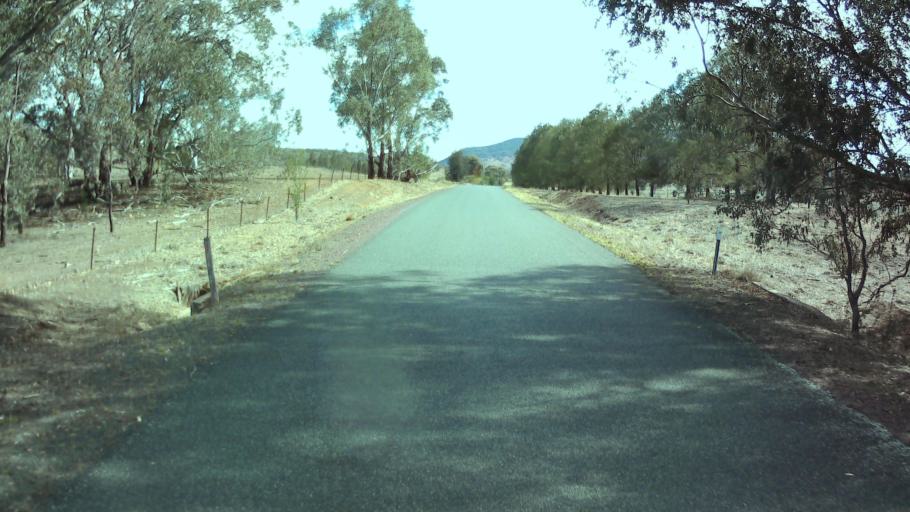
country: AU
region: New South Wales
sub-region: Weddin
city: Grenfell
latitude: -33.8115
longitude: 148.2926
